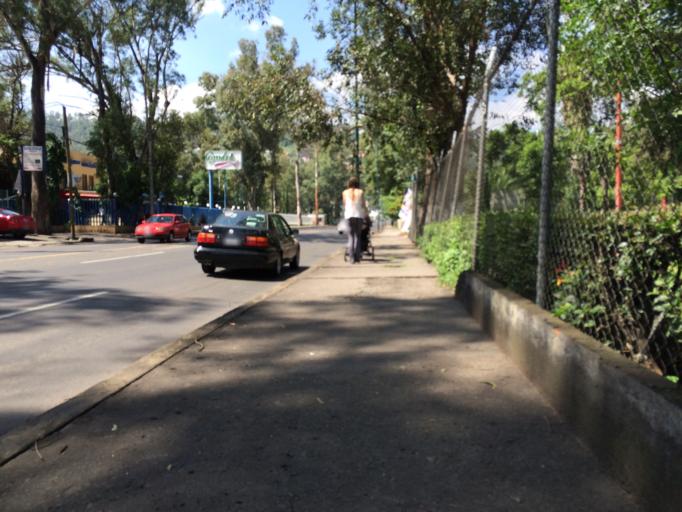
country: MX
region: Michoacan
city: Morelia
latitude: 19.6852
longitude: -101.1808
